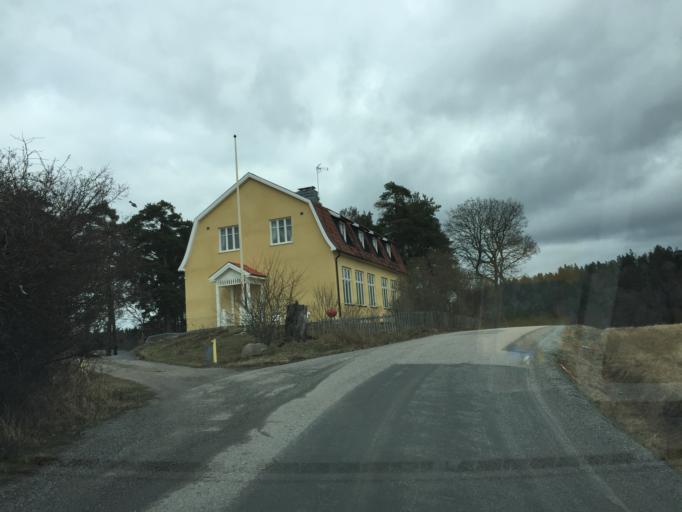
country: SE
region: Stockholm
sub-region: Salems Kommun
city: Ronninge
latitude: 59.2450
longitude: 17.6870
